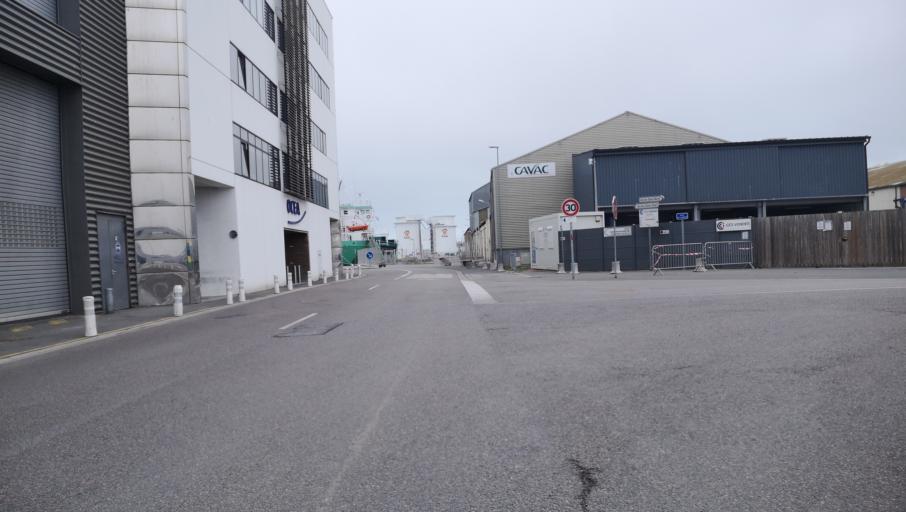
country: FR
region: Pays de la Loire
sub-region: Departement de la Vendee
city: Les Sables-d'Olonne
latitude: 46.4998
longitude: -1.7887
